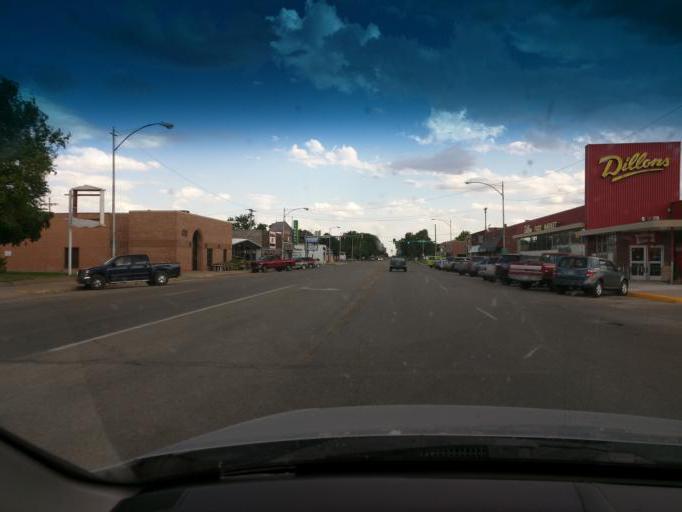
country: US
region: Kansas
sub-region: Reno County
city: Hutchinson
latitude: 38.0687
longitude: -97.9319
